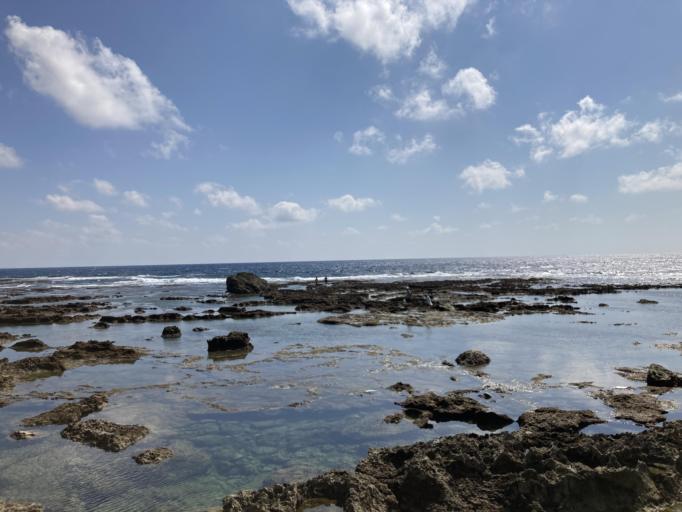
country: JP
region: Okinawa
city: Itoman
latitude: 26.1011
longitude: 127.7348
